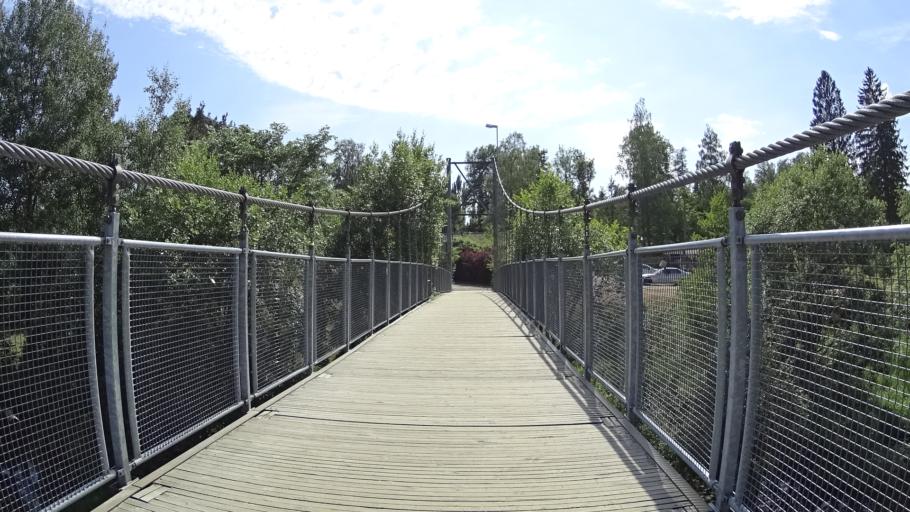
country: FI
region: Uusimaa
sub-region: Raaseporin
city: Karis
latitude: 60.0762
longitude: 23.6671
